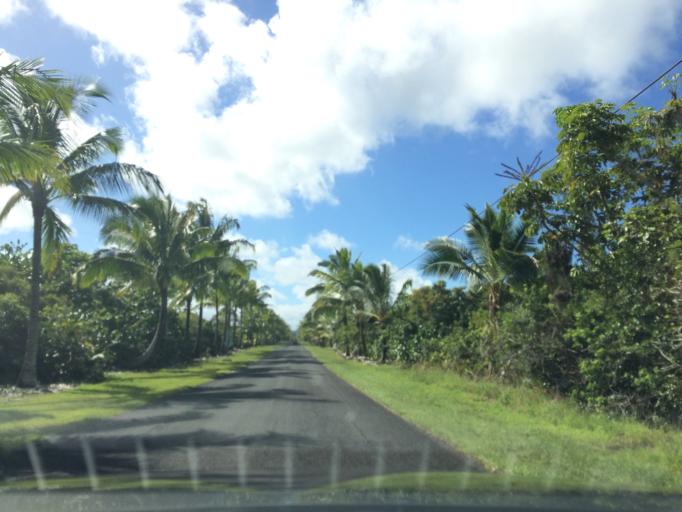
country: US
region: Hawaii
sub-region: Hawaii County
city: Nanawale Estates
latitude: 19.4919
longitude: -154.8248
